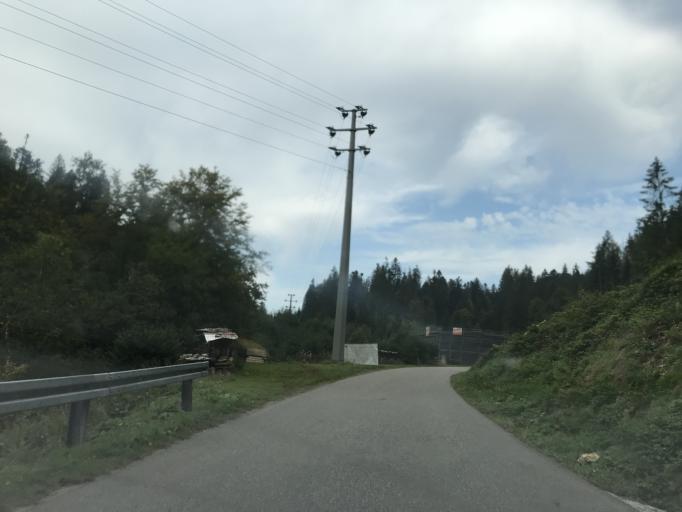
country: DE
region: Baden-Wuerttemberg
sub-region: Freiburg Region
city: Todtmoos
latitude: 47.7193
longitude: 7.9983
